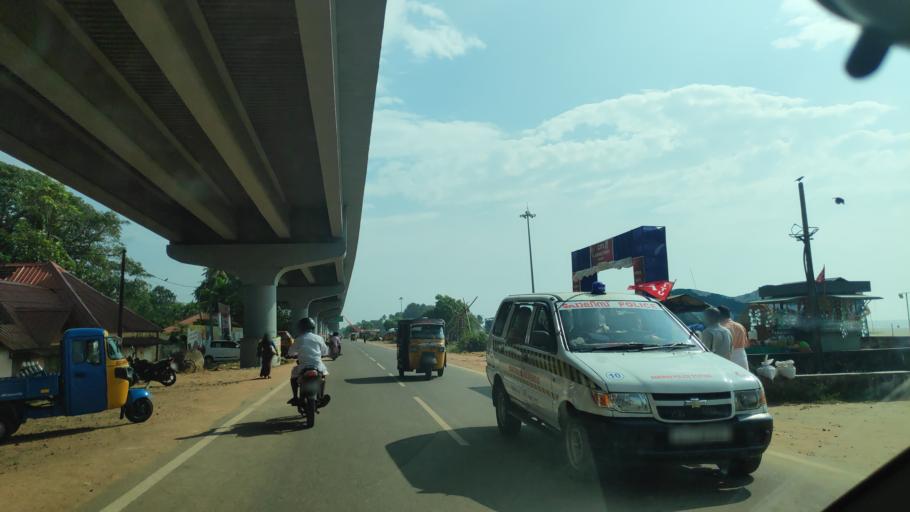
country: IN
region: Kerala
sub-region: Alappuzha
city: Alleppey
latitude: 9.4920
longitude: 76.3189
